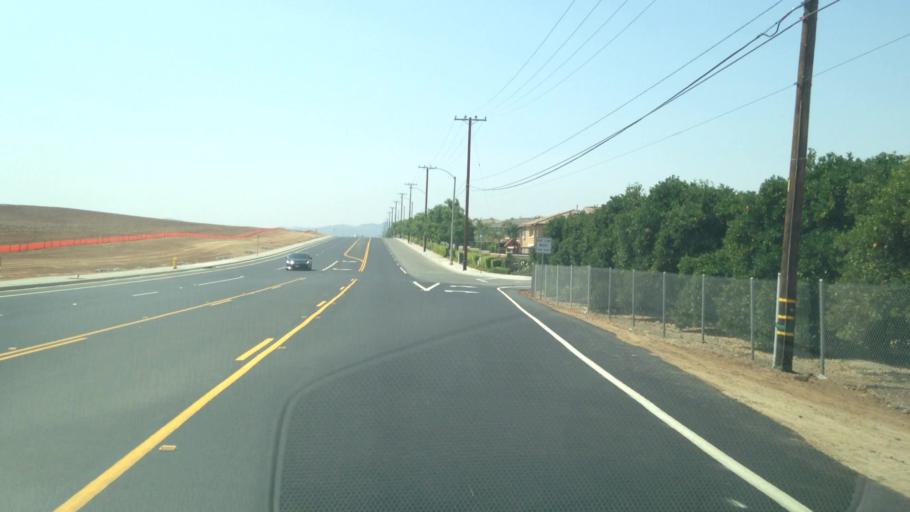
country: US
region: California
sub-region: Riverside County
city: Woodcrest
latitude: 33.8855
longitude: -117.3139
